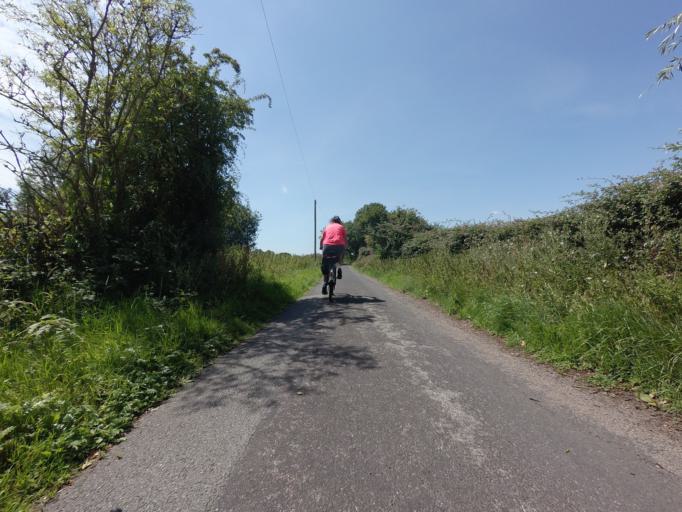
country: GB
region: England
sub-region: Kent
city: Stone
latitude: 50.9948
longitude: 0.8327
